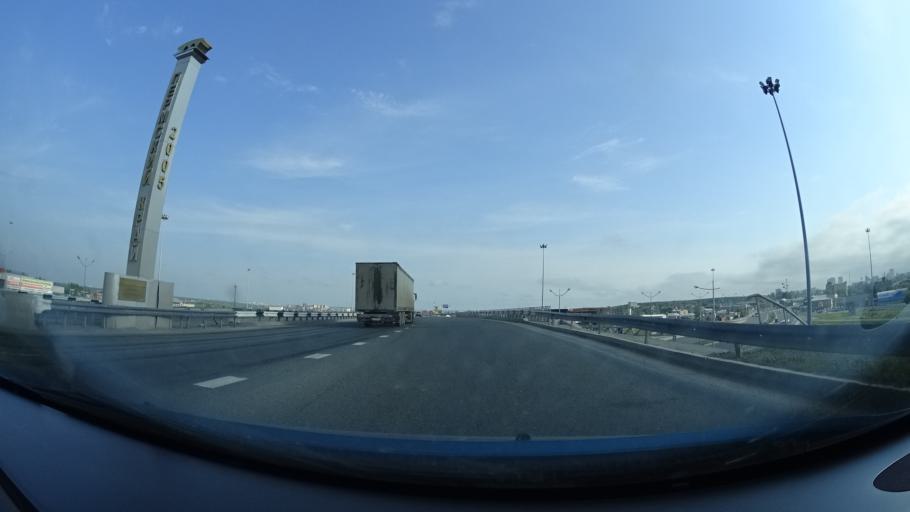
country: RU
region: Perm
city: Kondratovo
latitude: 57.9541
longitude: 56.1228
